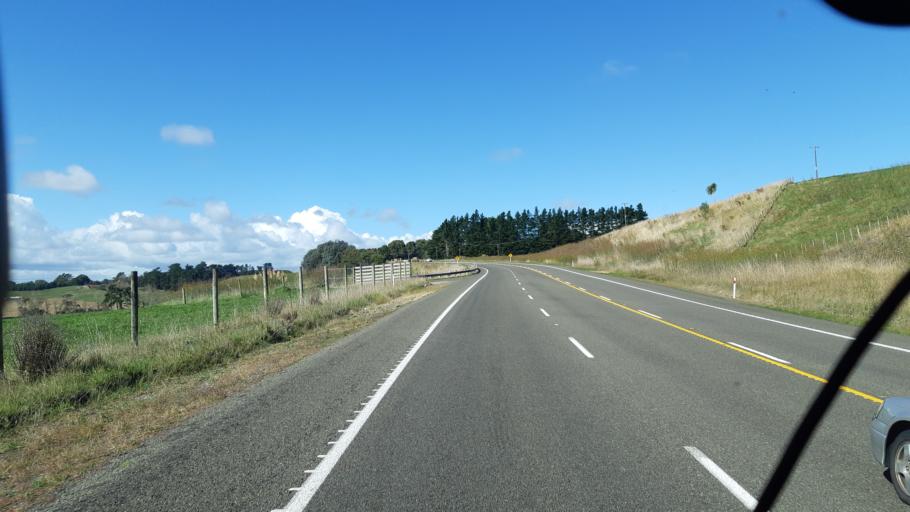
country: NZ
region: Manawatu-Wanganui
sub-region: Wanganui District
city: Wanganui
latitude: -39.9705
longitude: 175.1092
